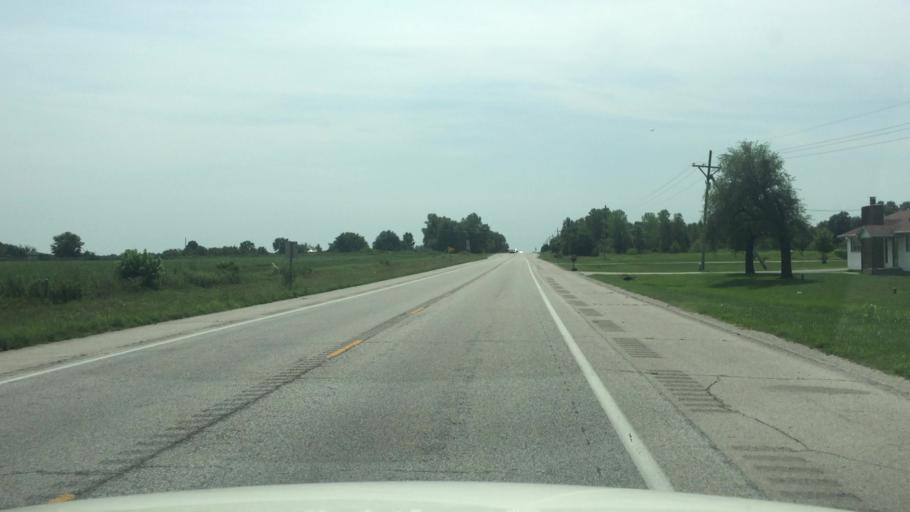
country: US
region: Kansas
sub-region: Cherokee County
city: Galena
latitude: 37.1081
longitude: -94.7044
